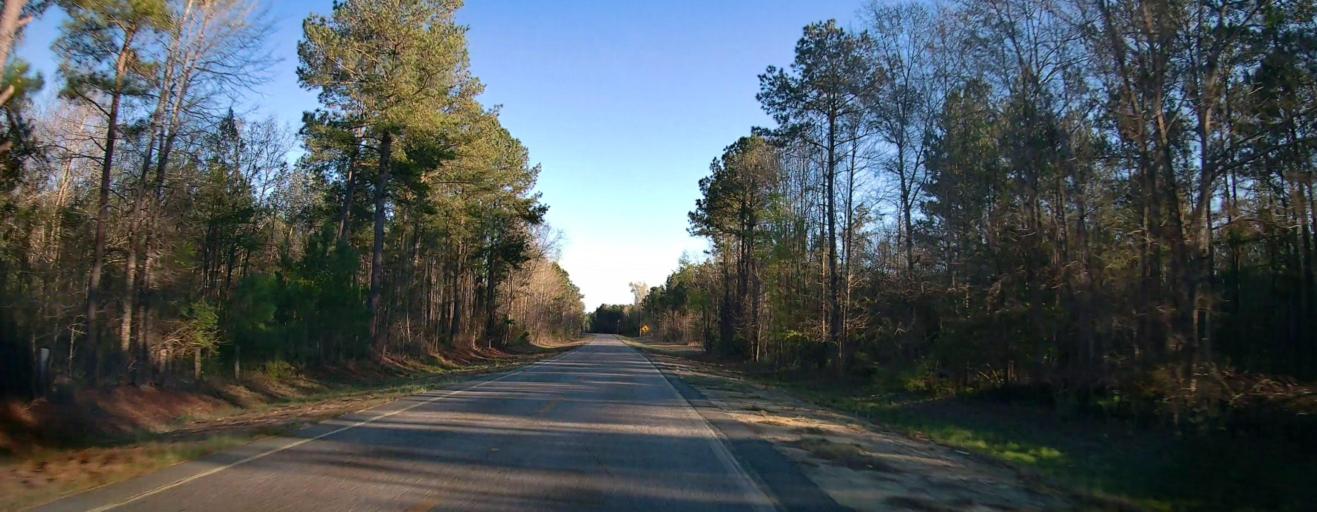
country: US
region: Georgia
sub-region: Wilcox County
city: Abbeville
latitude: 32.0742
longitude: -83.2850
